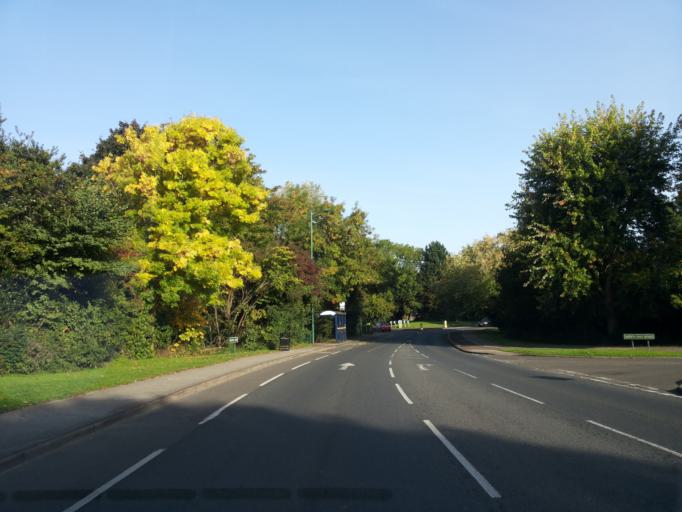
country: GB
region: England
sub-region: Solihull
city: Knowle
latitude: 52.3931
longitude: -1.7407
